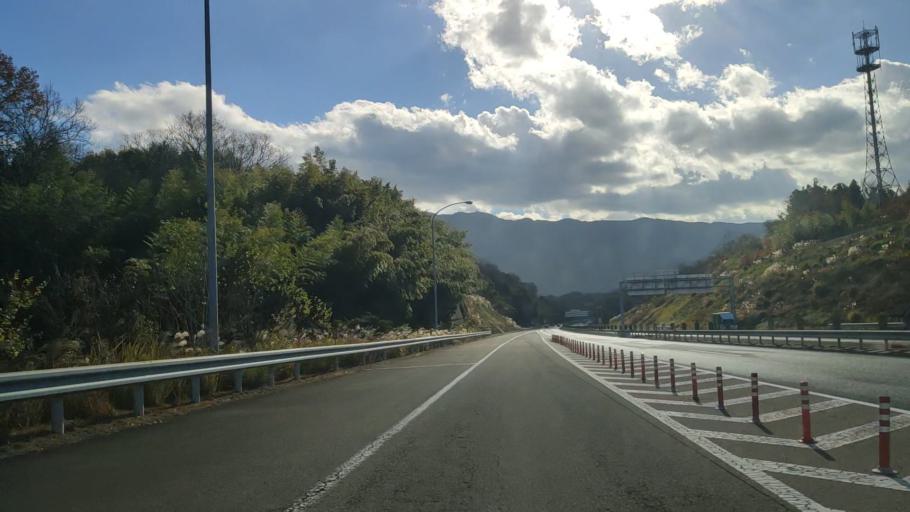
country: JP
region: Ehime
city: Kawanoecho
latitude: 33.9986
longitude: 133.5967
